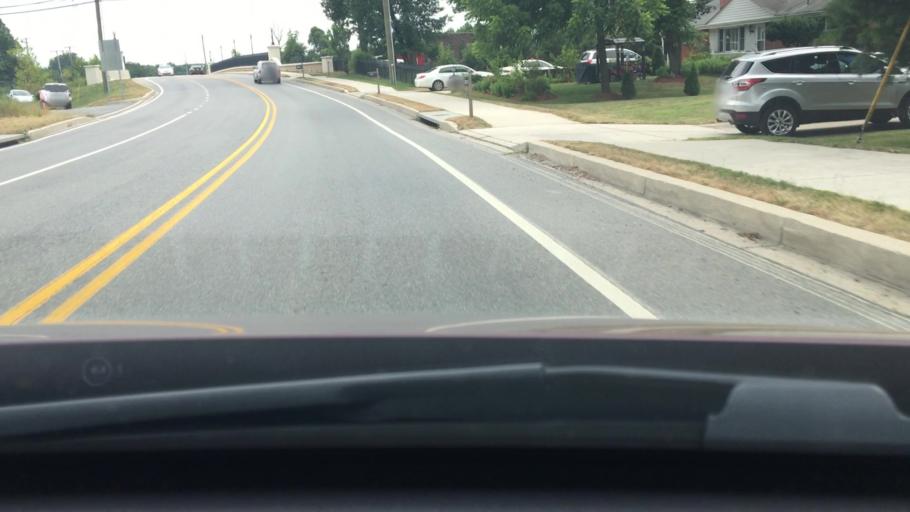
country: US
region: Maryland
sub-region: Prince George's County
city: Calverton
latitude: 39.0752
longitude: -76.9211
